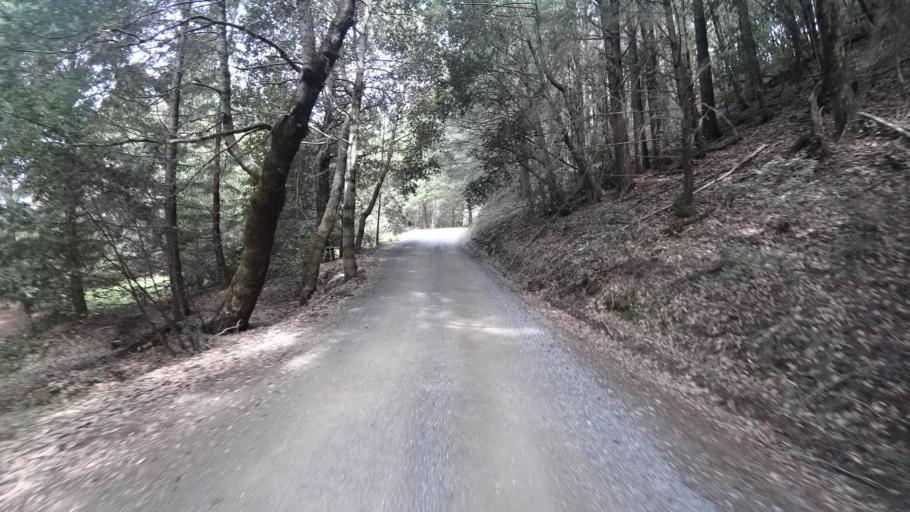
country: US
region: California
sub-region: Humboldt County
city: Redway
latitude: 40.0369
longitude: -123.8401
